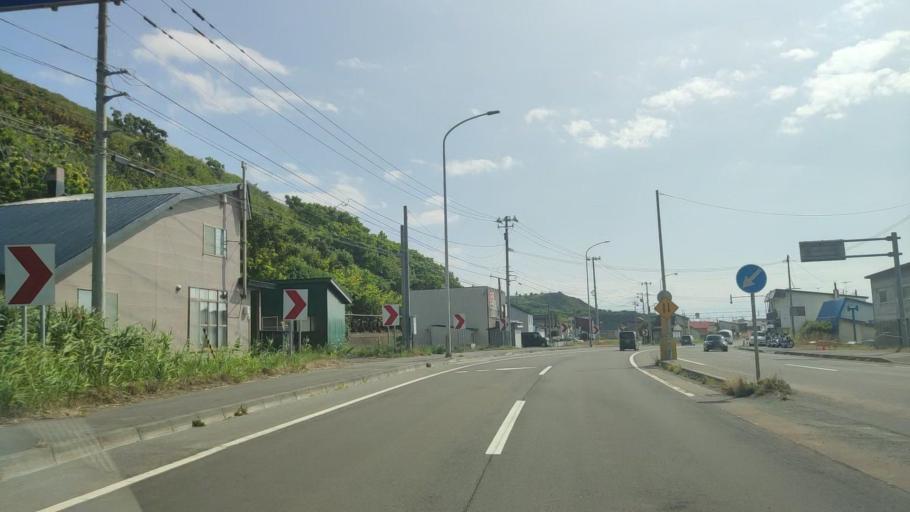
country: JP
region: Hokkaido
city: Rumoi
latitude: 44.0008
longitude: 141.6572
